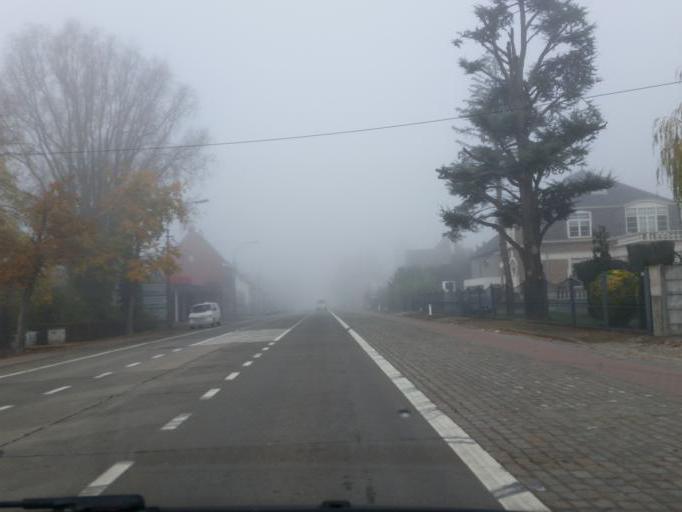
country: BE
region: Flanders
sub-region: Provincie Oost-Vlaanderen
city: Melle
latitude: 50.9928
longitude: 3.8267
